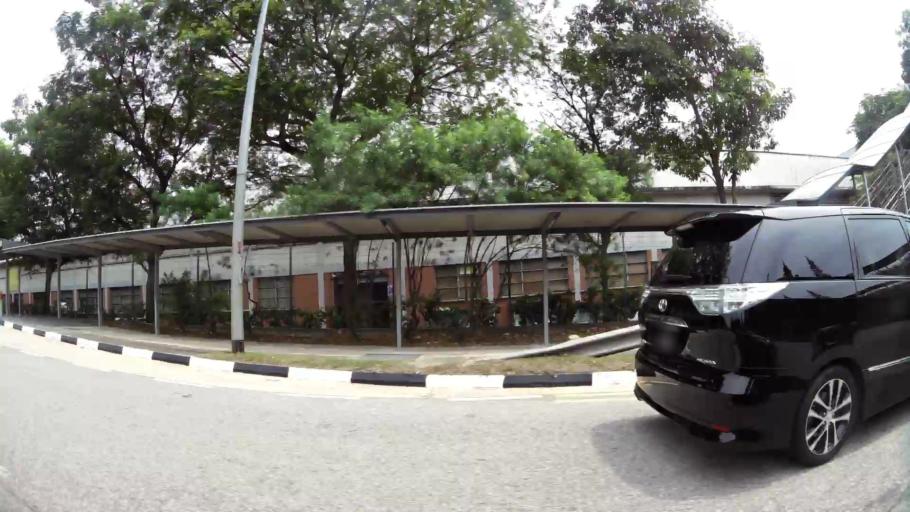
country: SG
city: Singapore
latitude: 1.3189
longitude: 103.7104
